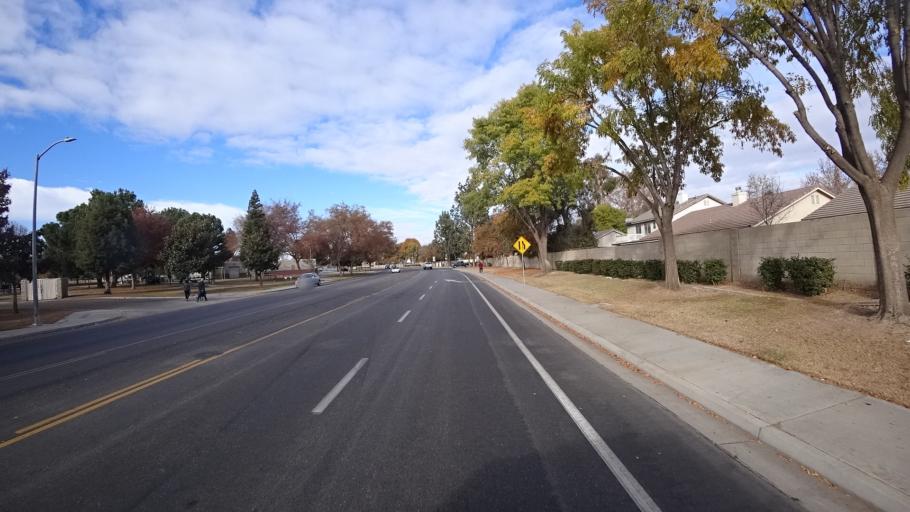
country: US
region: California
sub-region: Kern County
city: Greenacres
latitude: 35.3044
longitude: -119.0804
